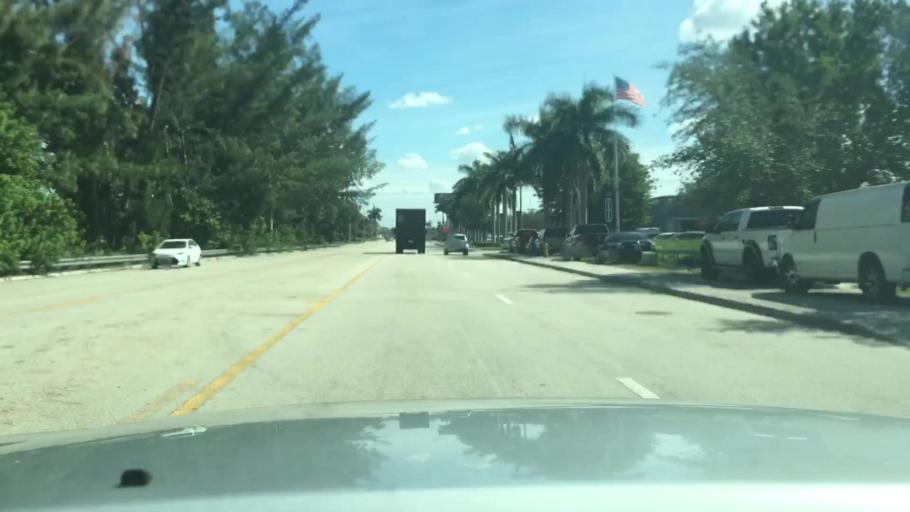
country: US
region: Florida
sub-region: Miami-Dade County
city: Fountainebleau
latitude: 25.7832
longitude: -80.3440
